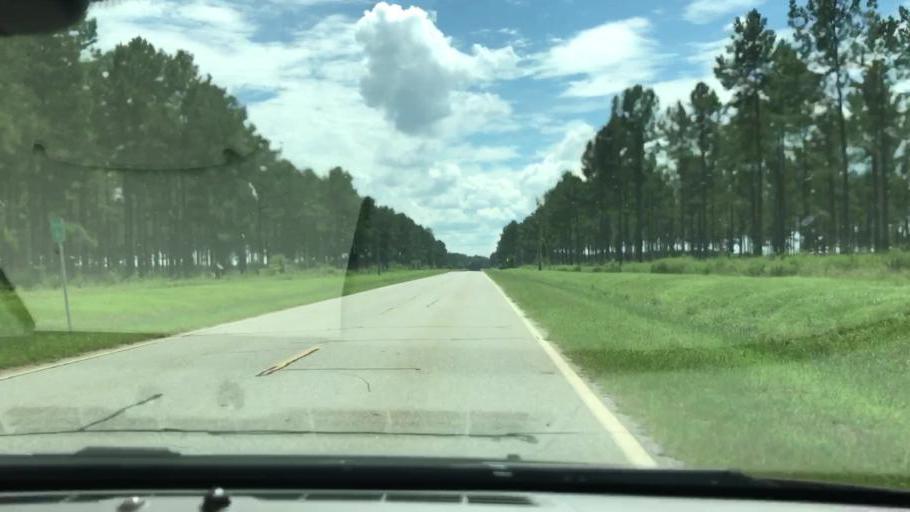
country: US
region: Georgia
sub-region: Quitman County
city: Georgetown
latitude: 32.0624
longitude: -85.0363
